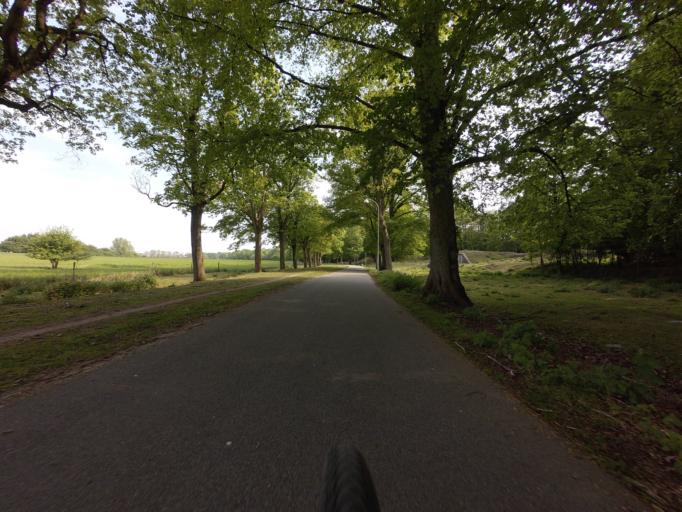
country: DK
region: Capital Region
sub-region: Brondby Kommune
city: Brondbyvester
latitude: 55.6356
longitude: 12.4328
